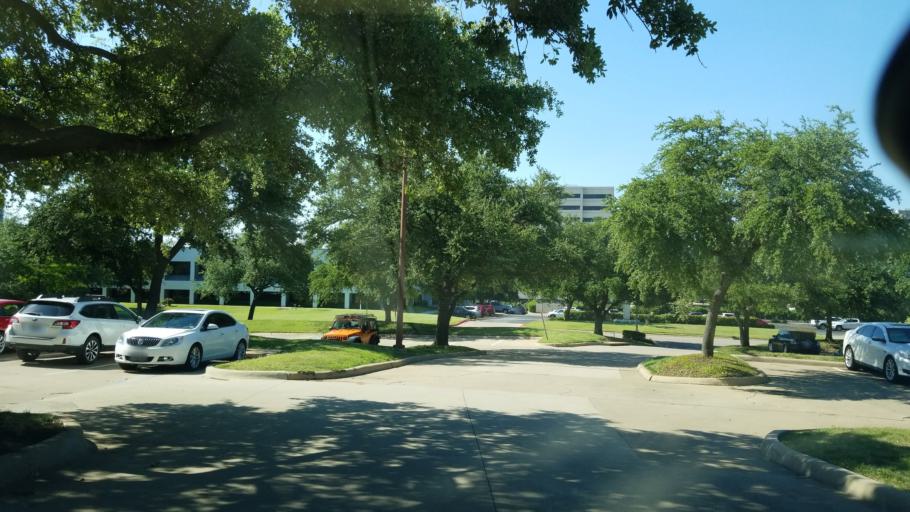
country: US
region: Texas
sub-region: Dallas County
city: Irving
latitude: 32.8868
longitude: -96.9699
